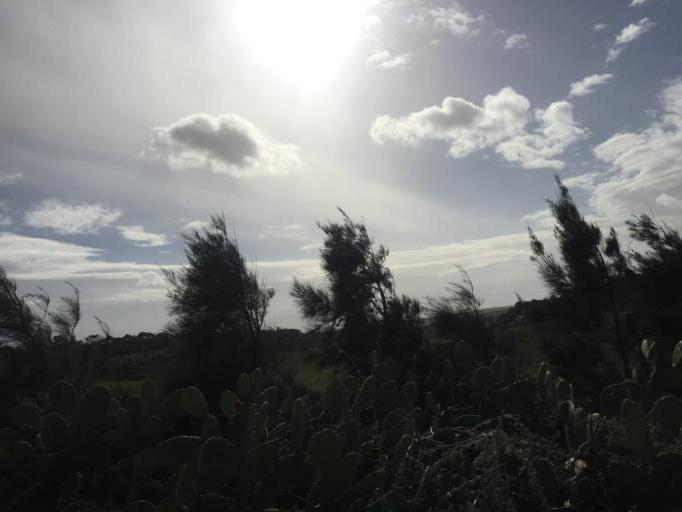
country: TN
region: Nabul
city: El Mida
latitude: 36.7980
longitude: 10.8449
